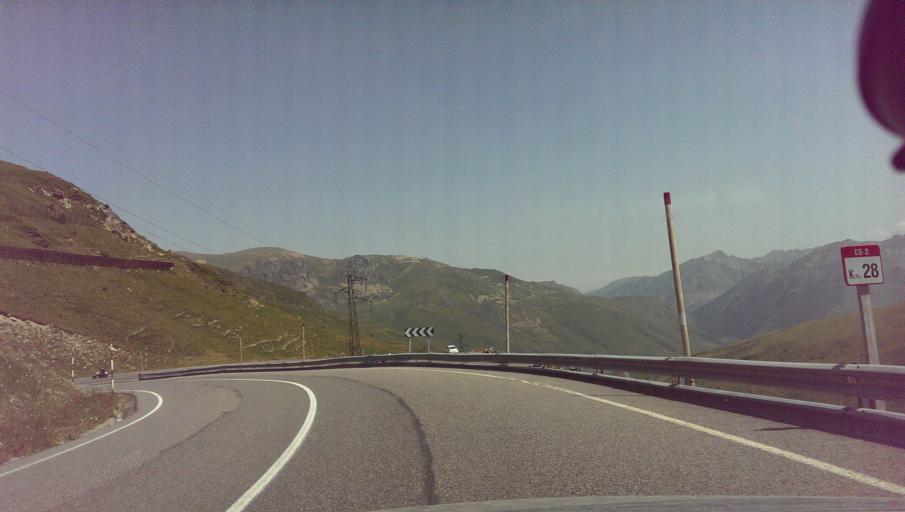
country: AD
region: Encamp
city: Pas de la Casa
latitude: 42.5408
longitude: 1.7247
